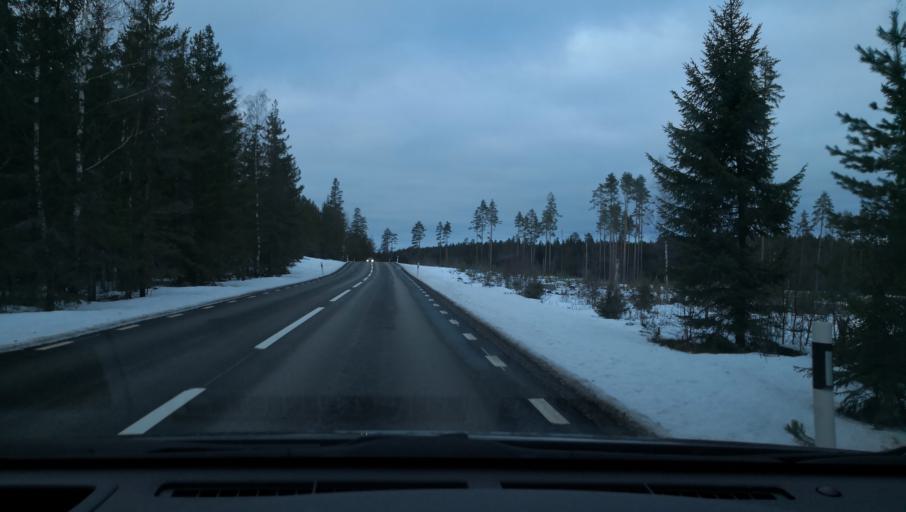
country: SE
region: Vaestmanland
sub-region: Skinnskattebergs Kommun
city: Skinnskatteberg
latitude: 59.8211
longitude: 15.8368
